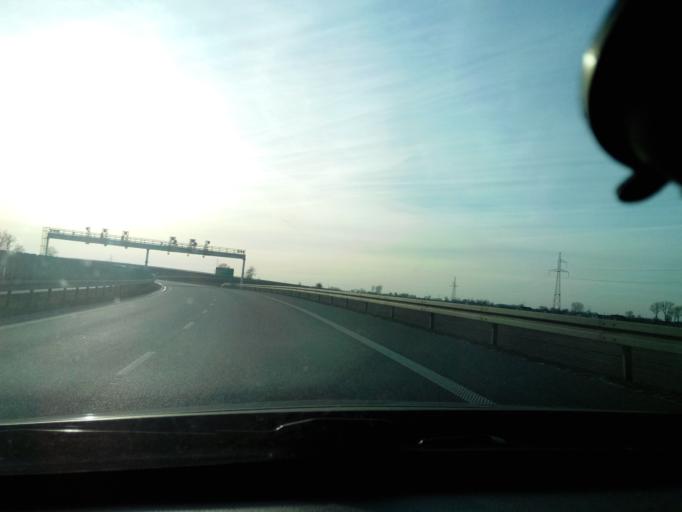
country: PL
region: Lodz Voivodeship
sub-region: Powiat kutnowski
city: Krosniewice
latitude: 52.2682
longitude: 19.1731
